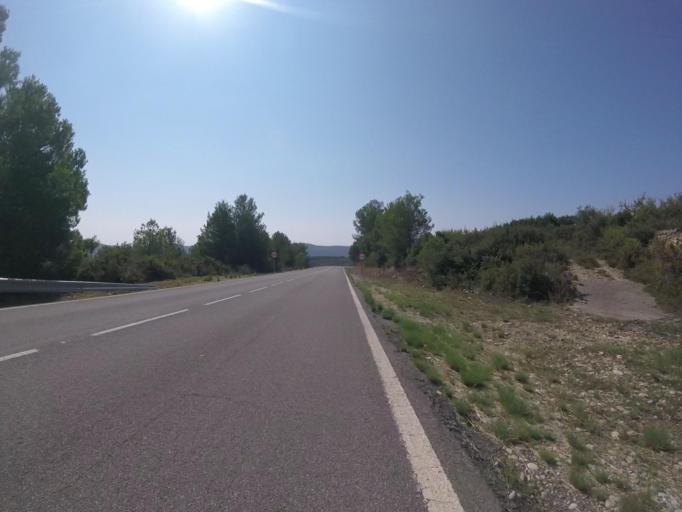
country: ES
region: Valencia
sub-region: Provincia de Castello
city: Adzaneta
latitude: 40.2405
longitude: -0.1886
